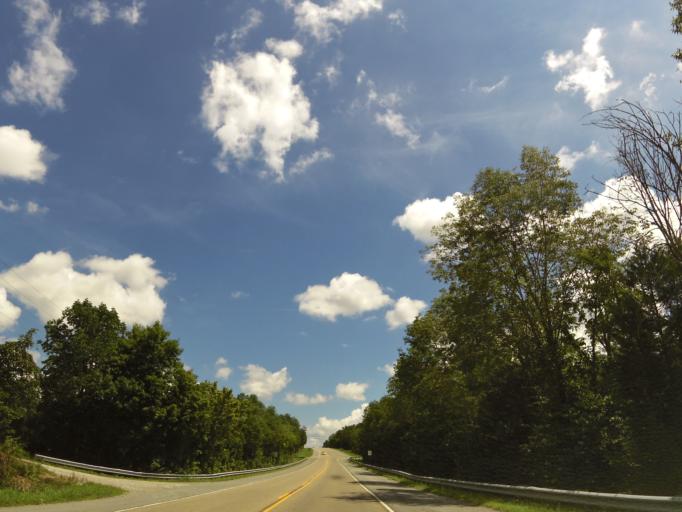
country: US
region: Tennessee
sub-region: Claiborne County
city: Harrogate
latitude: 36.5354
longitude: -83.6936
